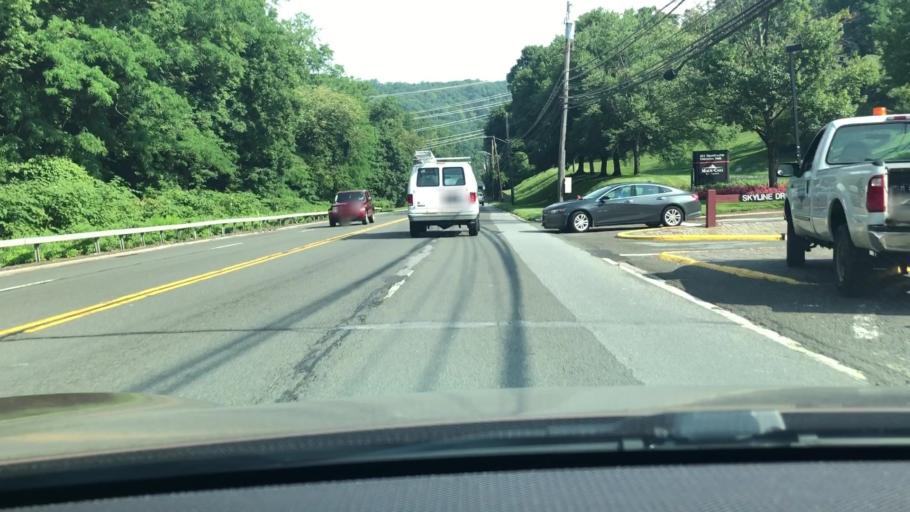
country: US
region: New York
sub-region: Westchester County
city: Elmsford
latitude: 41.0850
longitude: -73.8191
